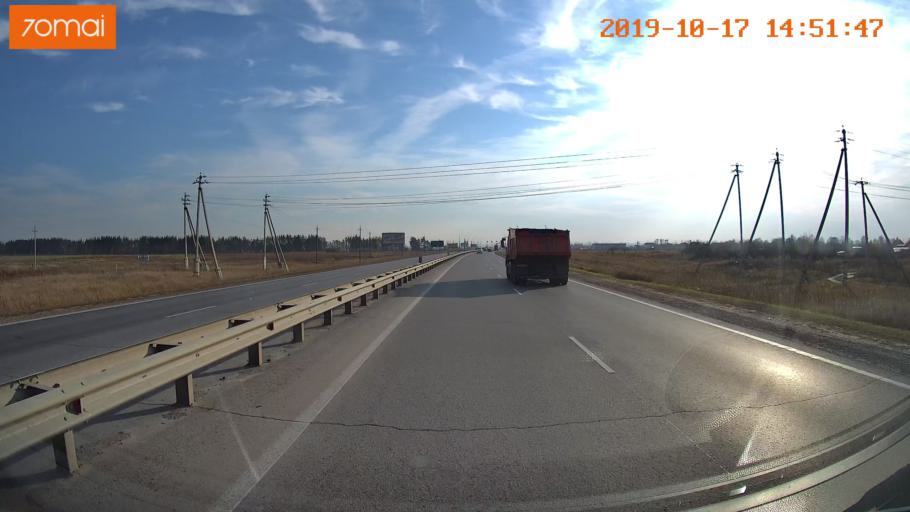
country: RU
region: Rjazan
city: Polyany
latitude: 54.7138
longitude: 39.8480
